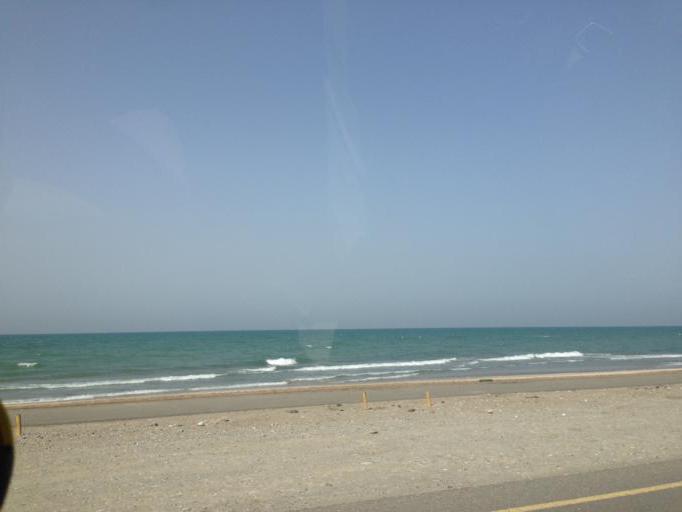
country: OM
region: Al Batinah
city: Barka'
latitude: 23.7247
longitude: 57.8472
